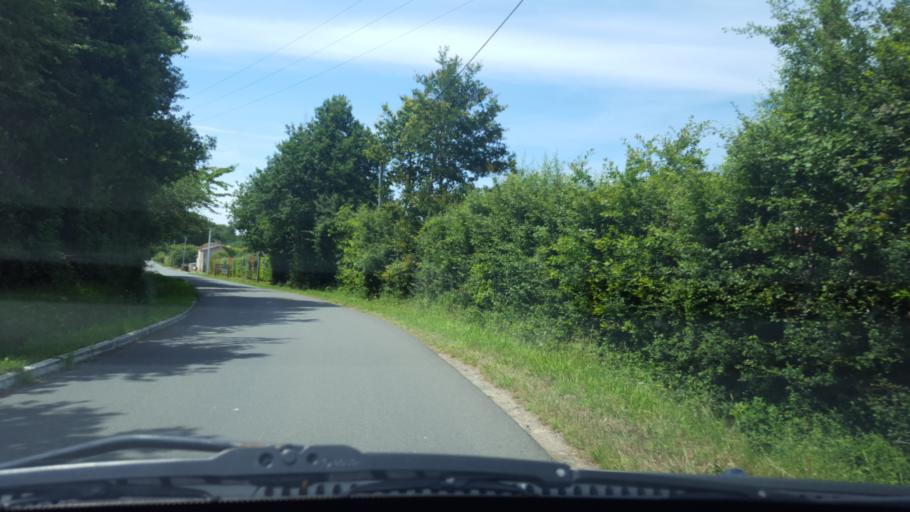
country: FR
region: Pays de la Loire
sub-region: Departement de la Loire-Atlantique
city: La Limouziniere
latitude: 47.0250
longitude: -1.5912
